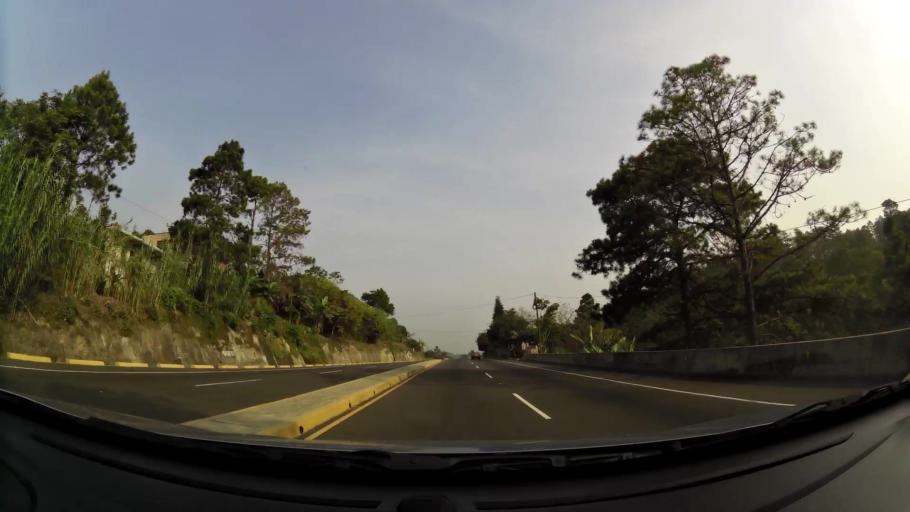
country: HN
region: Francisco Morazan
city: Zambrano
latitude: 14.2695
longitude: -87.4016
